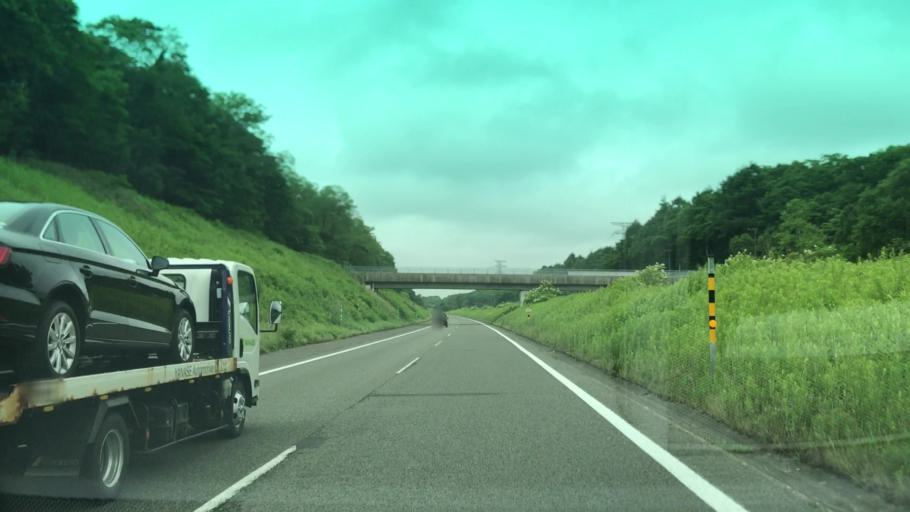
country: JP
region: Hokkaido
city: Chitose
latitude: 42.7309
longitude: 141.6529
